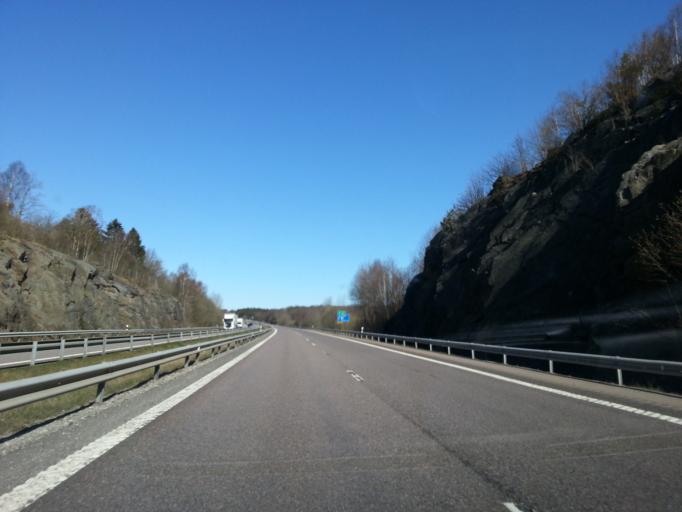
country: SE
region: Vaestra Goetaland
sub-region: Kungalvs Kommun
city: Kode
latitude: 57.9316
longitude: 11.8728
